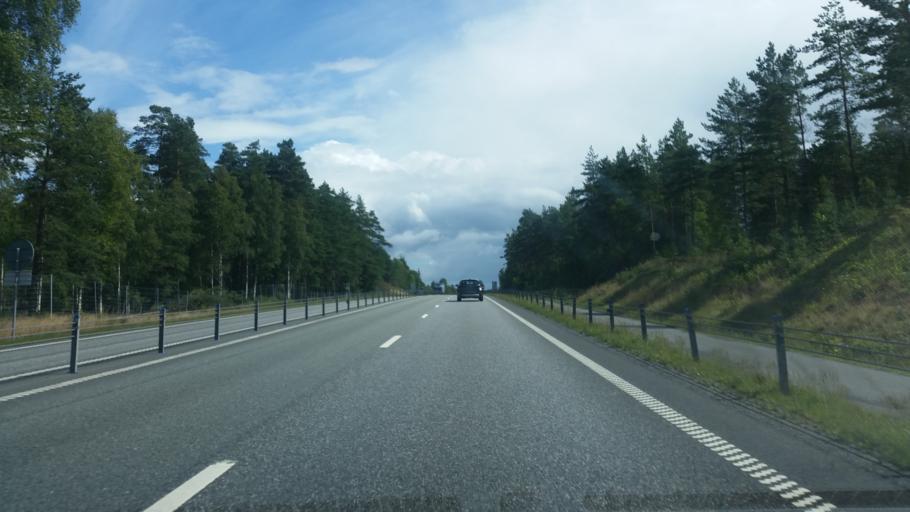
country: SE
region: Joenkoeping
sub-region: Mullsjo Kommun
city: Mullsjoe
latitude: 57.7673
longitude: 13.7858
